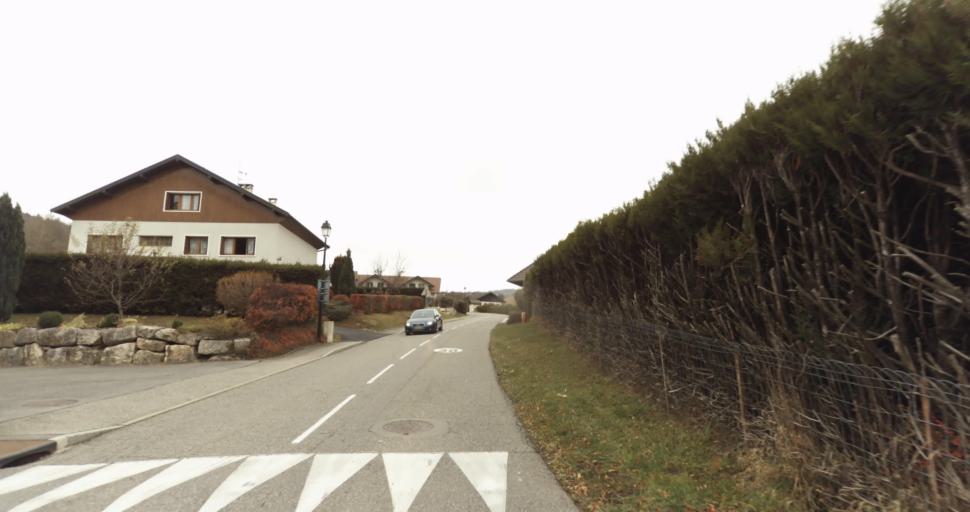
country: FR
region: Rhone-Alpes
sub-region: Departement de la Haute-Savoie
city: Saint-Martin-Bellevue
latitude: 45.9637
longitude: 6.1642
